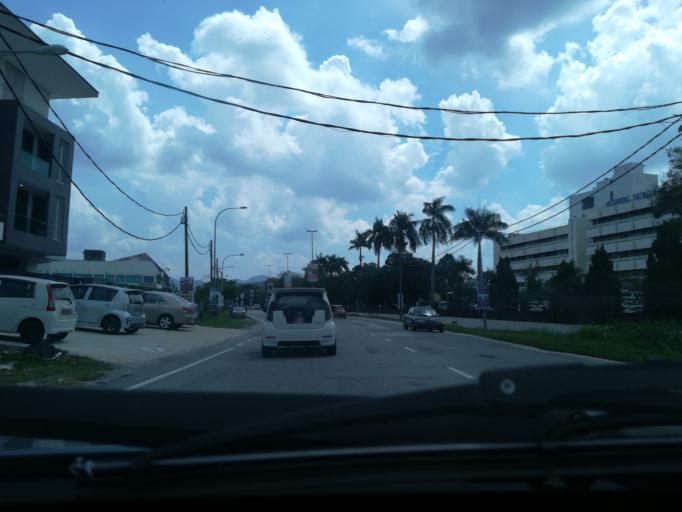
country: MY
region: Perak
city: Ipoh
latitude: 4.6124
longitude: 101.1133
